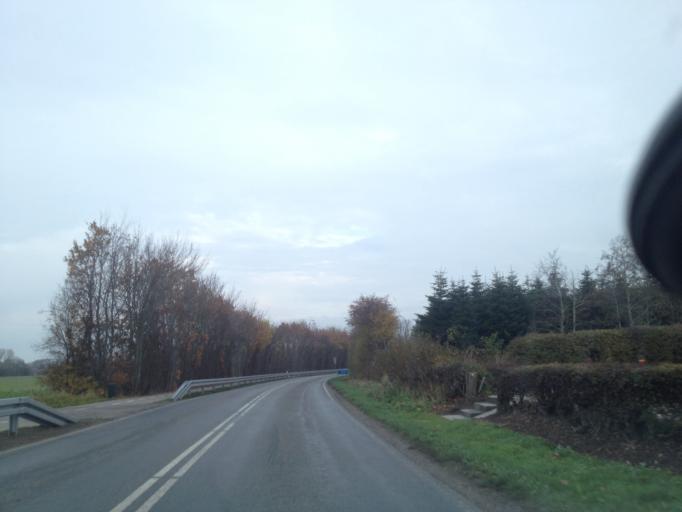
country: DK
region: South Denmark
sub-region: Nordfyns Kommune
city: Bogense
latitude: 55.5371
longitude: 10.0964
